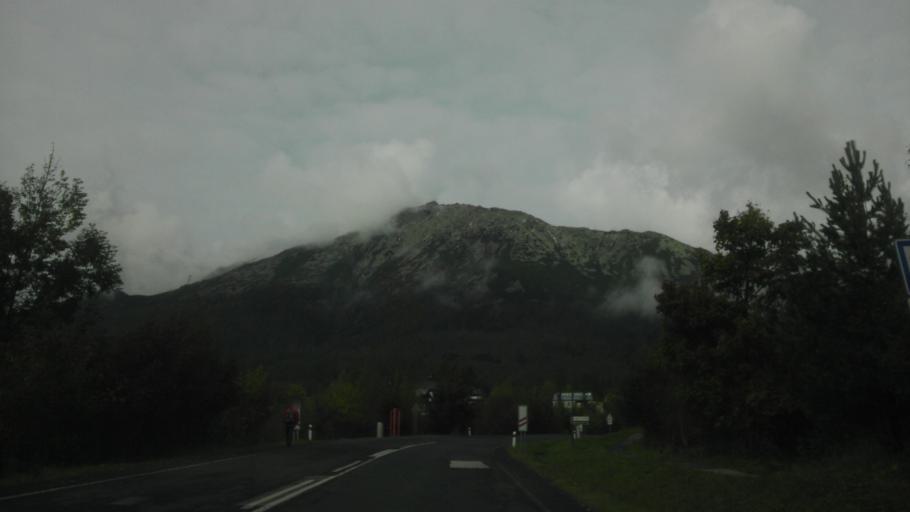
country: SK
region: Presovsky
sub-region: Okres Poprad
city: Vysoke Tatry
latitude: 49.1380
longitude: 20.2275
